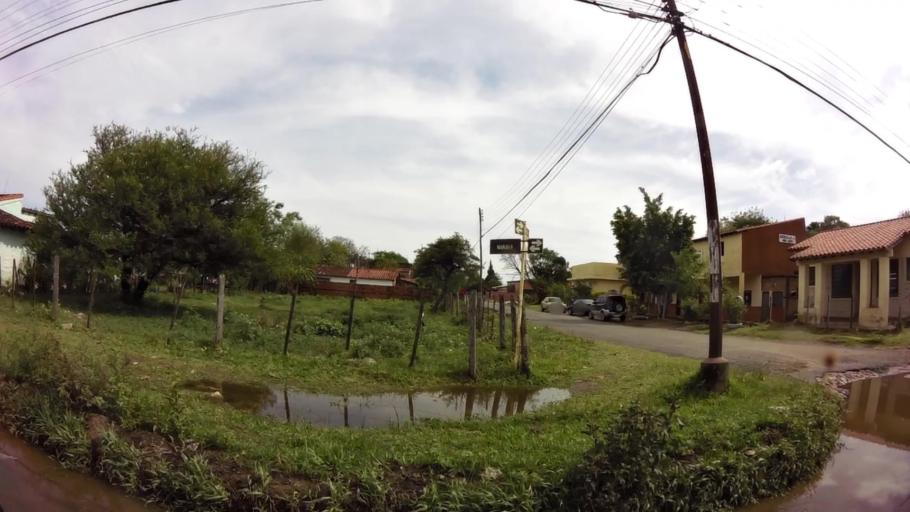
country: PY
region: Central
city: Limpio
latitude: -25.1757
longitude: -57.4788
